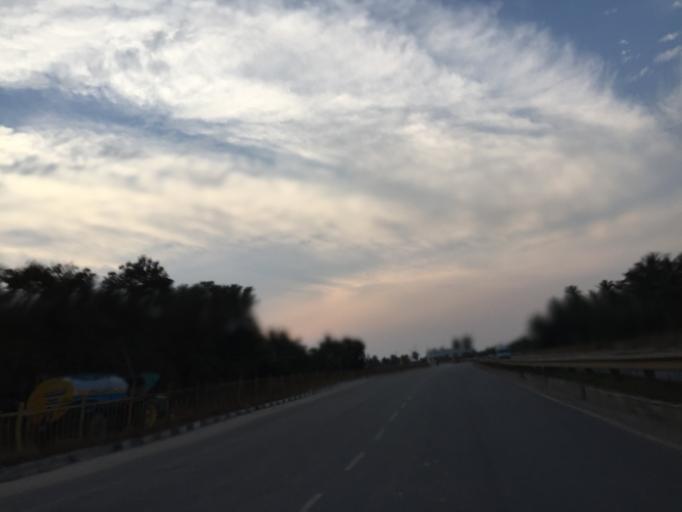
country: IN
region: Karnataka
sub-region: Bangalore Rural
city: Dasarahalli
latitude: 13.1201
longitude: 77.8947
